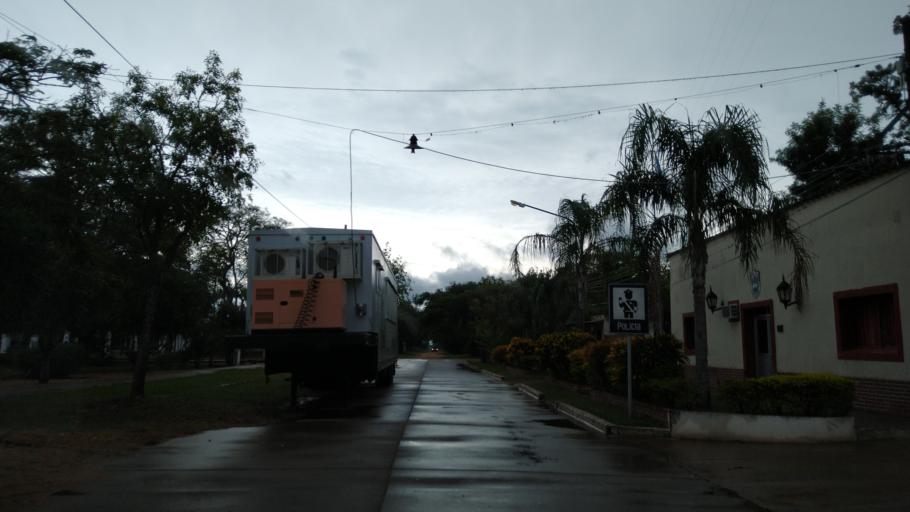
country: AR
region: Corrientes
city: Loreto
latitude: -27.7700
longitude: -57.2802
